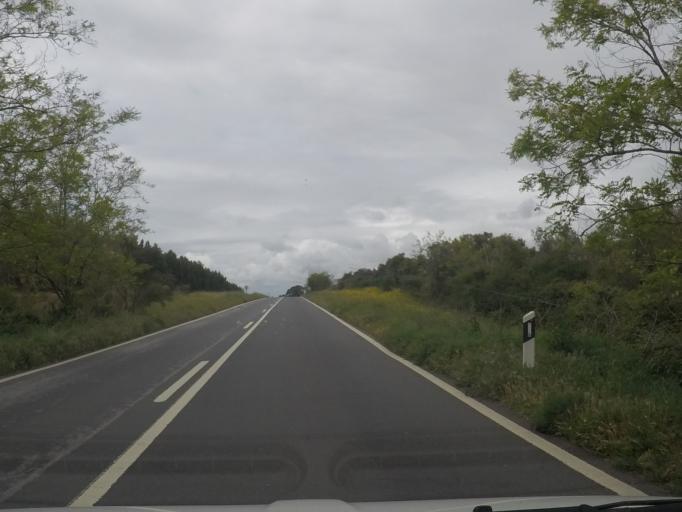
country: PT
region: Setubal
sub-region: Santiago do Cacem
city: Cercal
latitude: 37.8465
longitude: -8.7076
